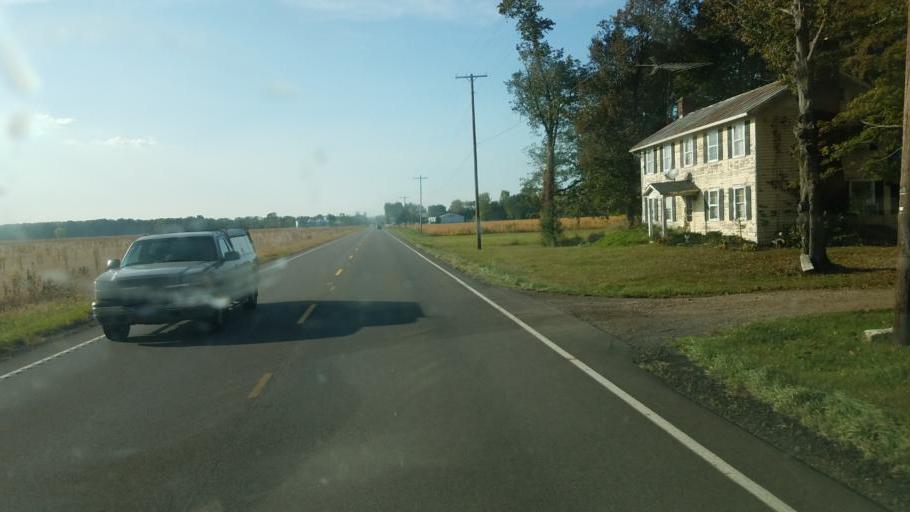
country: US
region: Ohio
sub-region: Knox County
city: Fredericktown
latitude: 40.4464
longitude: -82.5323
